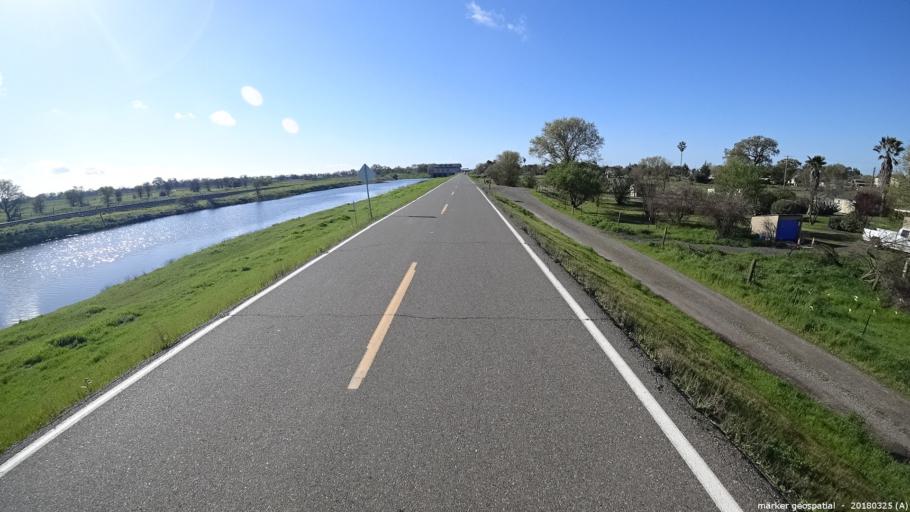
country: US
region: California
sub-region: Sacramento County
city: Rio Linda
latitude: 38.6695
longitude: -121.4780
